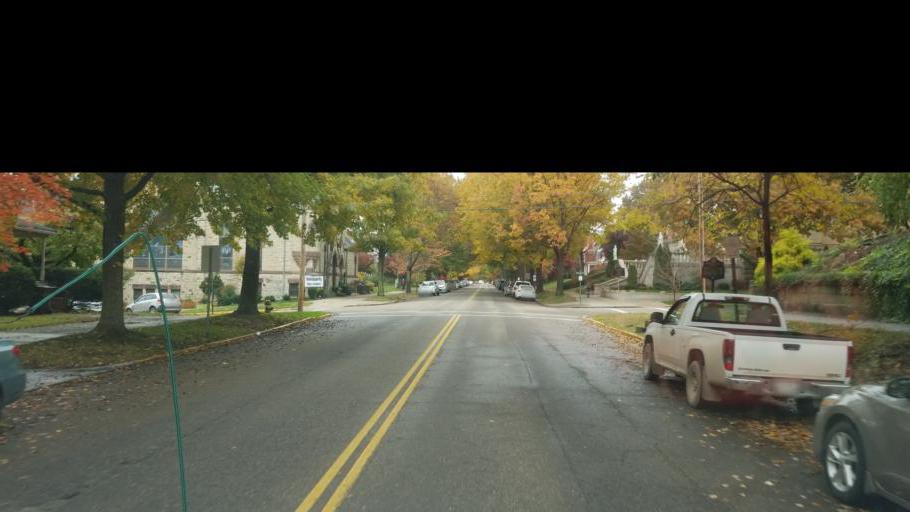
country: US
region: Ohio
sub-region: Washington County
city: Marietta
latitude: 39.4206
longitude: -81.4557
